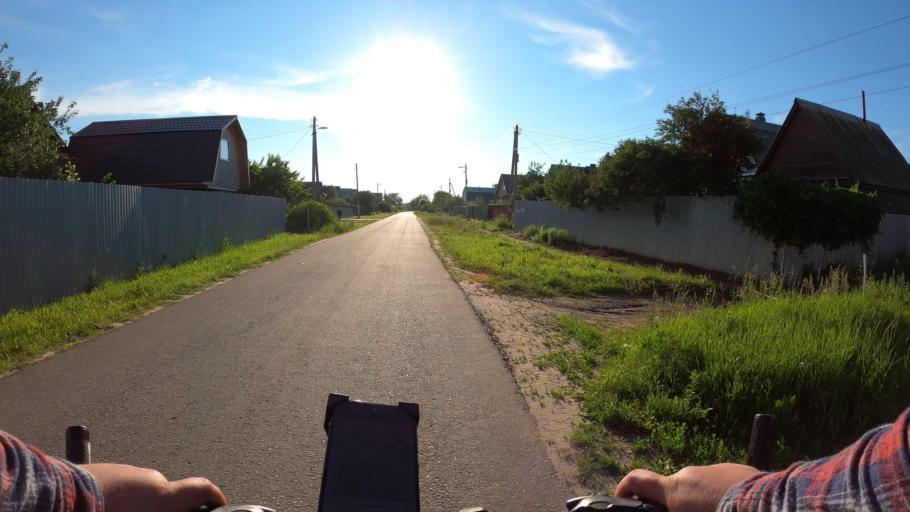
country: RU
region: Moskovskaya
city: Ashitkovo
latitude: 55.4545
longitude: 38.5901
